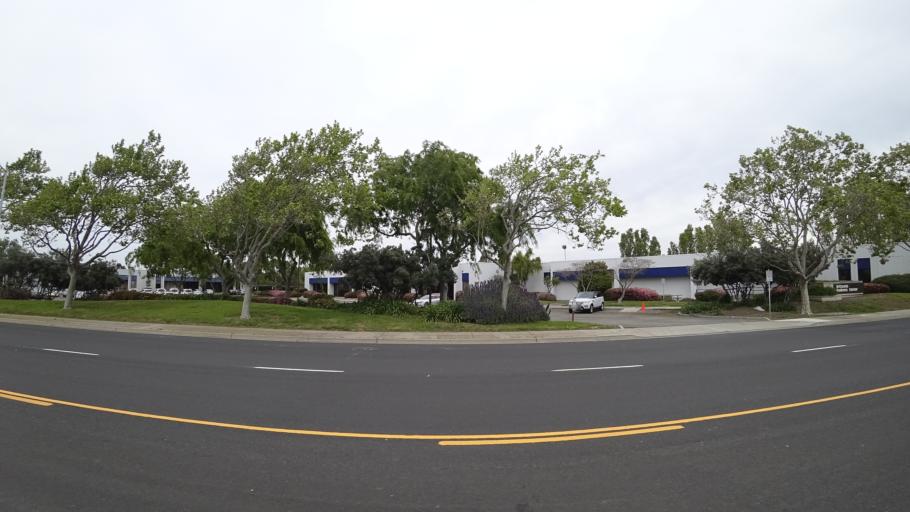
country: US
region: California
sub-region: Alameda County
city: San Lorenzo
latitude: 37.6418
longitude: -122.1363
